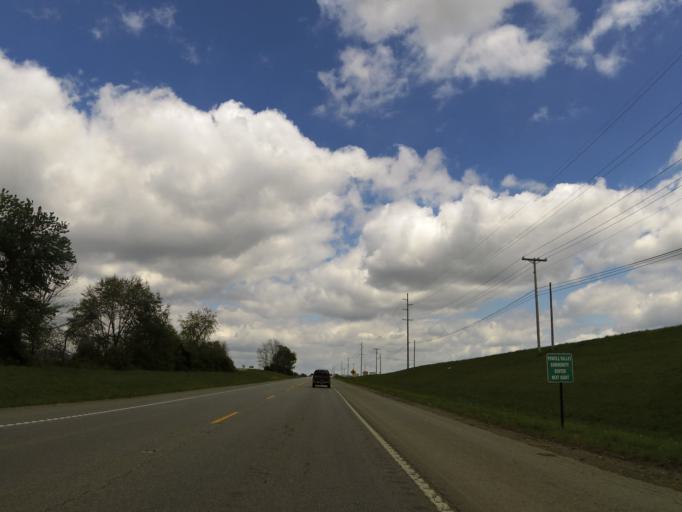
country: US
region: Kentucky
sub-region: Bell County
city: Middlesboro
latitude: 36.5083
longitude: -83.7903
